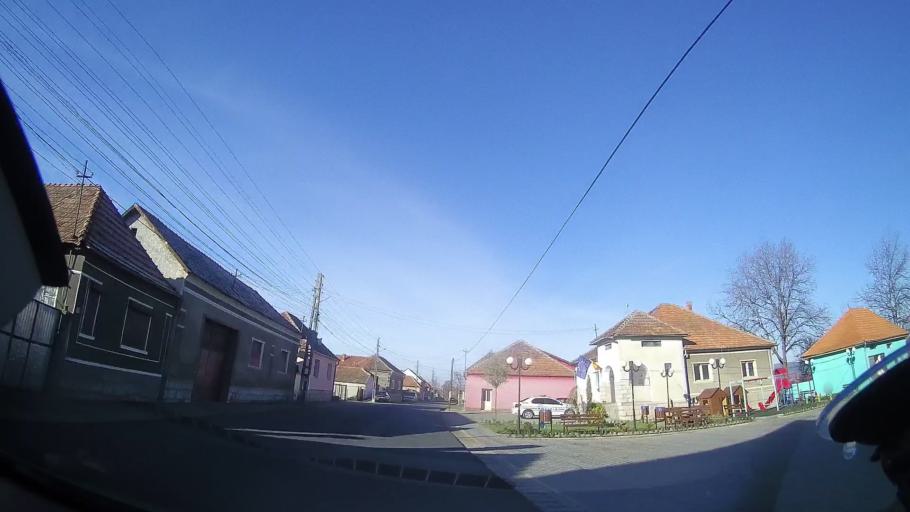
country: RO
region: Bihor
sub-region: Comuna Vadu Crisului
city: Vadu Crisului
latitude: 46.9875
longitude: 22.5128
